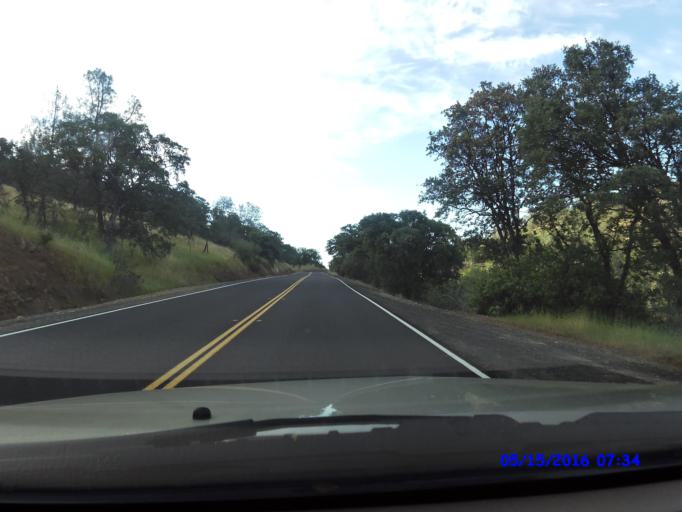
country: US
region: California
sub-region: Tuolumne County
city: Tuolumne City
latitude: 37.6848
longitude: -120.1759
